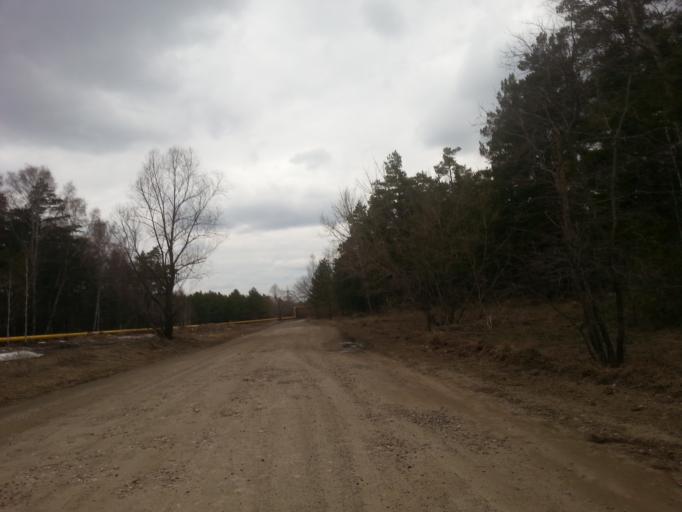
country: RU
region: Altai Krai
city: Yuzhnyy
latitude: 53.2836
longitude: 83.7322
